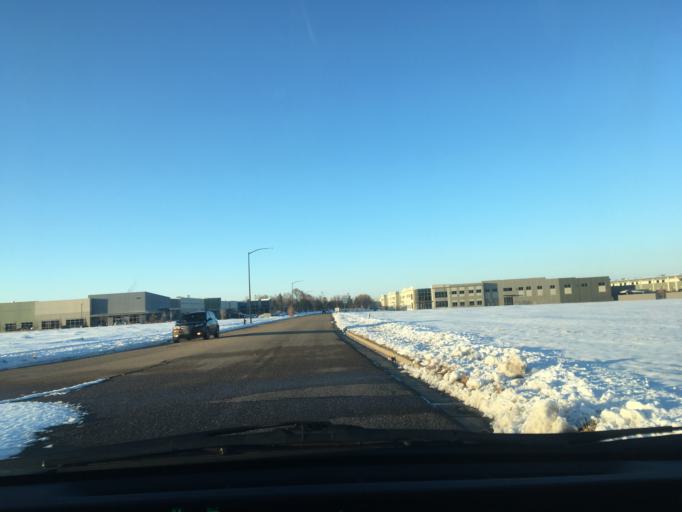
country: US
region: Colorado
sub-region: Boulder County
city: Louisville
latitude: 39.9583
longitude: -105.1127
